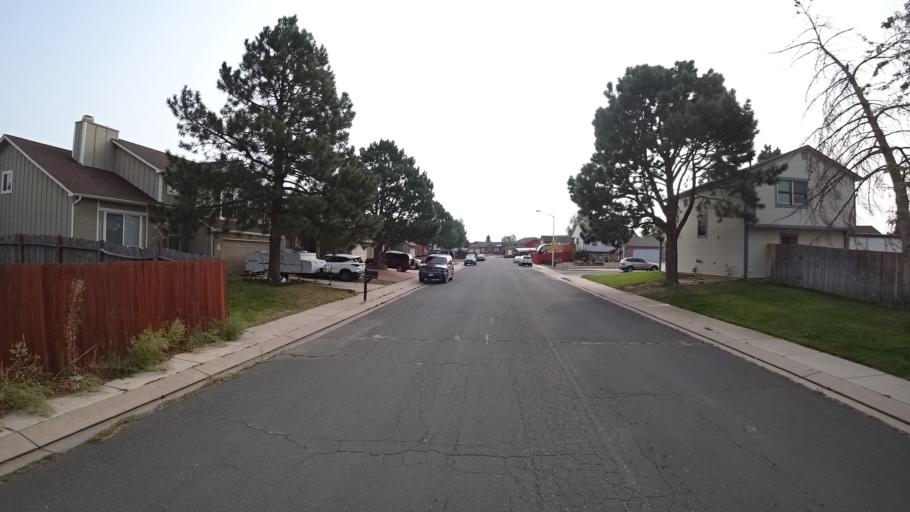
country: US
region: Colorado
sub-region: El Paso County
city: Stratmoor
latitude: 38.8085
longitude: -104.7475
